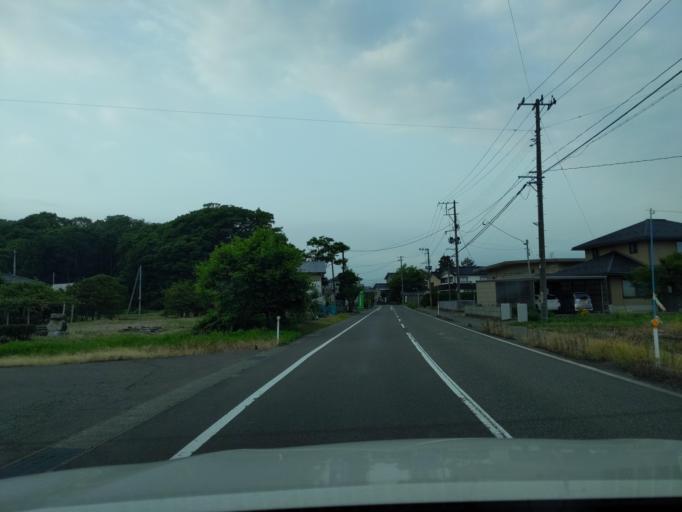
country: JP
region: Niigata
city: Kashiwazaki
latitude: 37.4205
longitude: 138.6165
